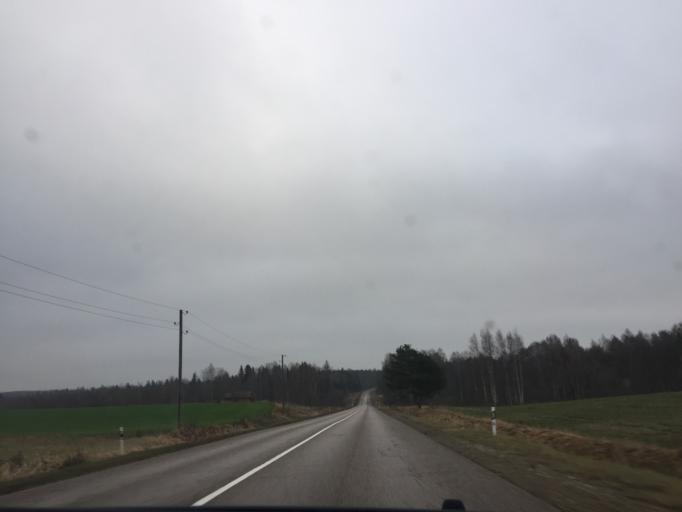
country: LV
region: Burtnieki
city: Matisi
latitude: 57.5160
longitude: 25.1462
